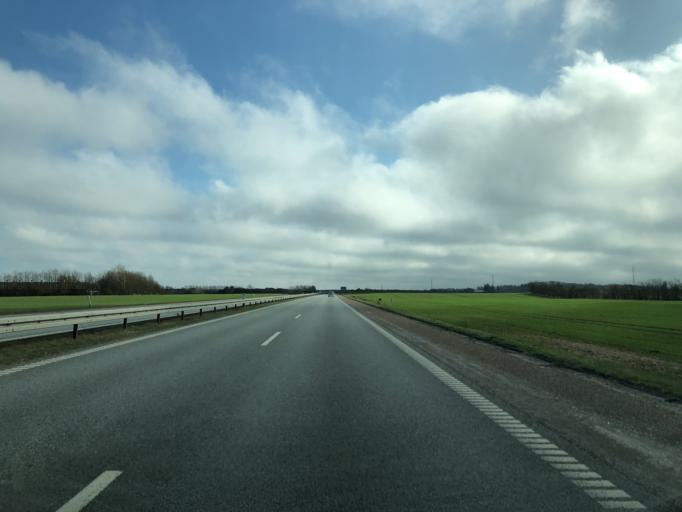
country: DK
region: North Denmark
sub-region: Hjorring Kommune
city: Hjorring
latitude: 57.4408
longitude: 10.0384
